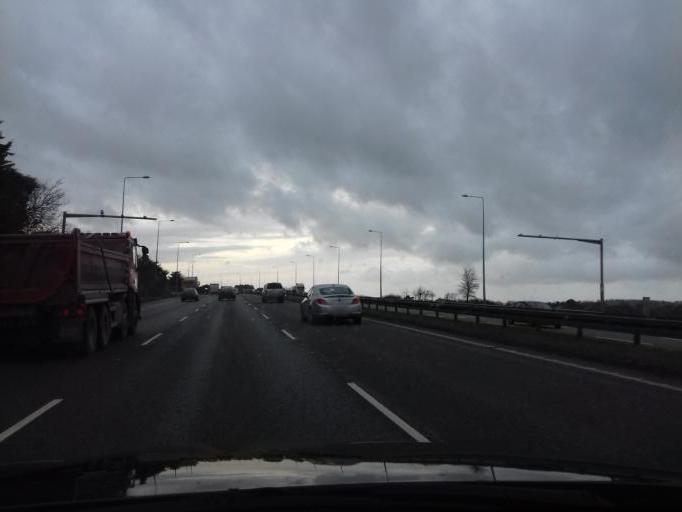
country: IE
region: Leinster
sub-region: South Dublin
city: Newcastle
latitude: 53.2764
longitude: -6.5004
